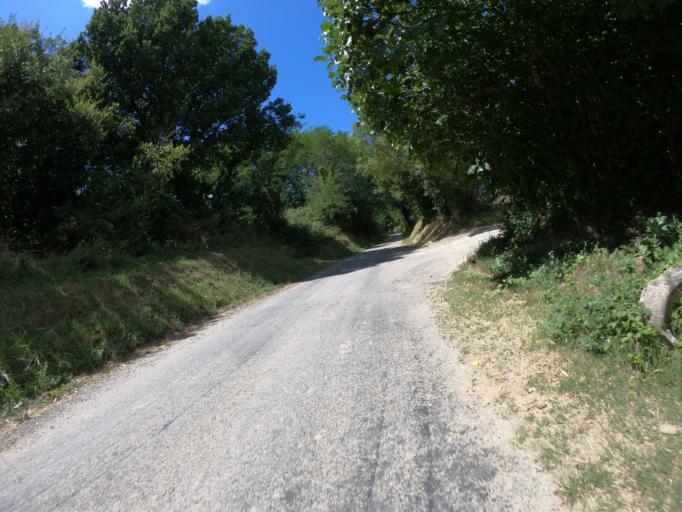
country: FR
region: Midi-Pyrenees
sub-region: Departement de l'Ariege
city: Verniolle
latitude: 43.0778
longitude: 1.7327
